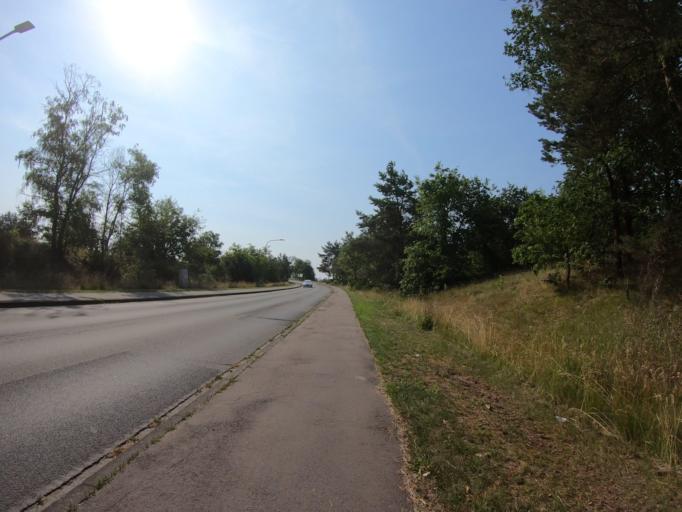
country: DE
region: Lower Saxony
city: Gifhorn
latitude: 52.4841
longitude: 10.5301
